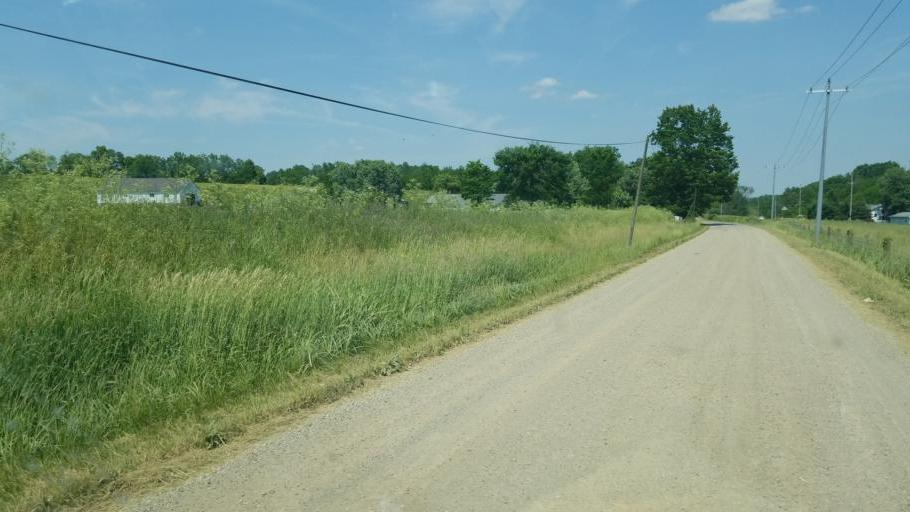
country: US
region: Ohio
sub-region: Knox County
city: Danville
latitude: 40.5412
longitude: -82.3372
